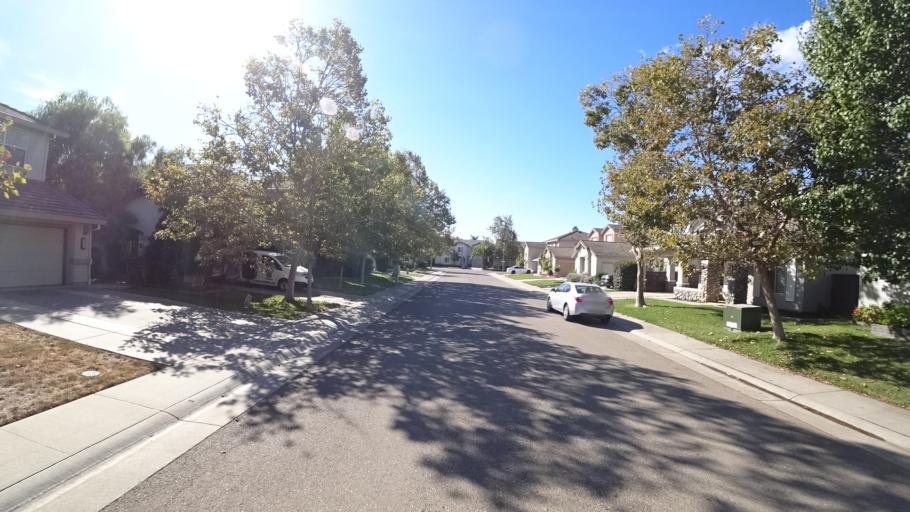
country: US
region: California
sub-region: Sacramento County
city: Laguna
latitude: 38.4207
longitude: -121.4841
